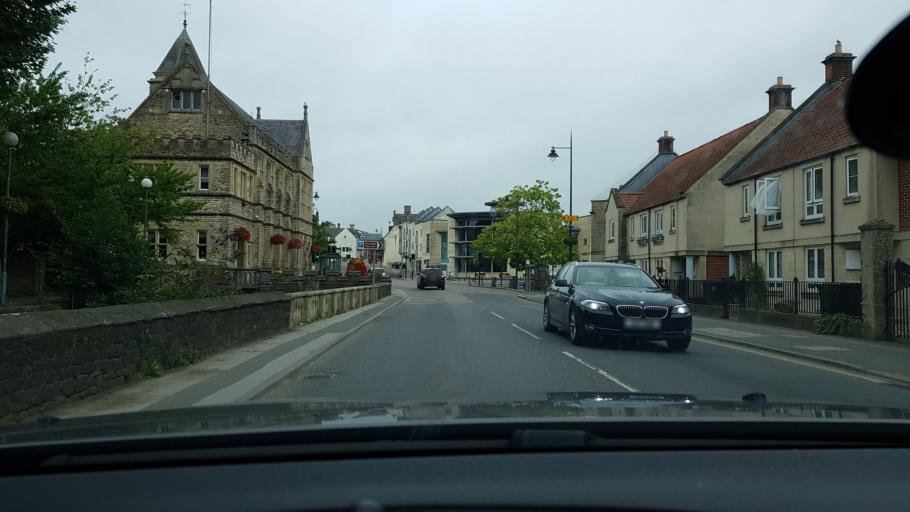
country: GB
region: England
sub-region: Wiltshire
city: Calne
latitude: 51.4371
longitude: -2.0048
